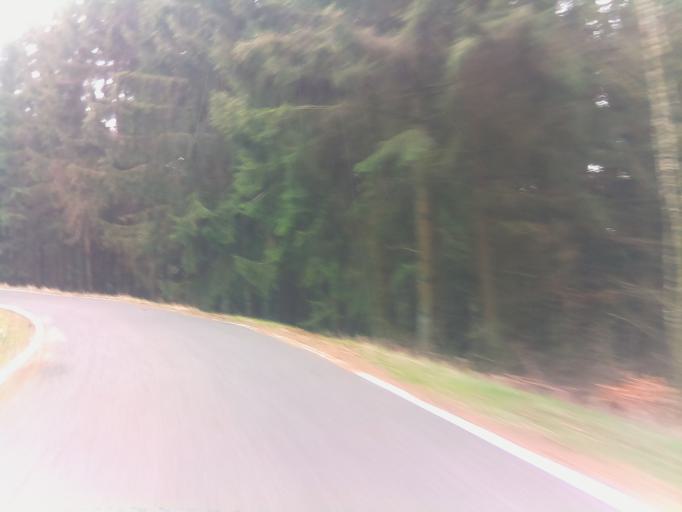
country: DE
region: Rheinland-Pfalz
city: Oberheimbach
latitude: 49.9893
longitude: 7.7740
